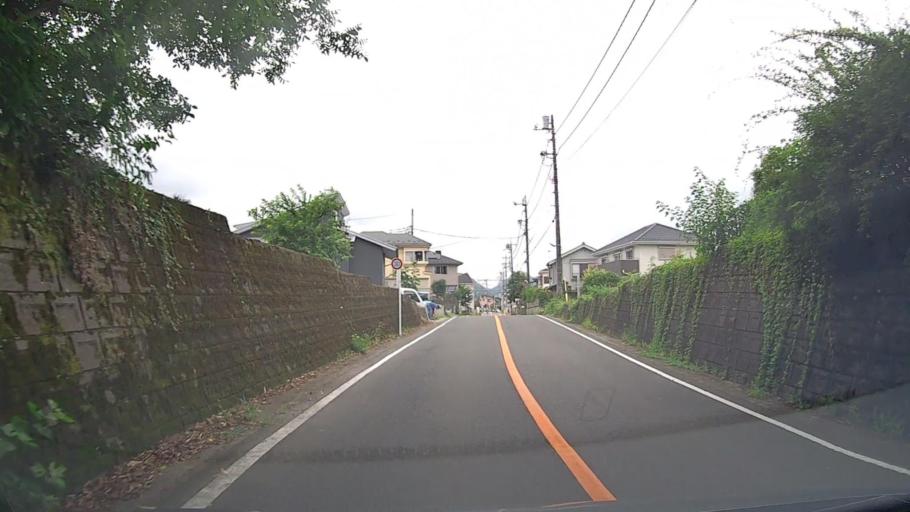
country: JP
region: Tokyo
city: Itsukaichi
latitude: 35.7225
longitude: 139.2347
